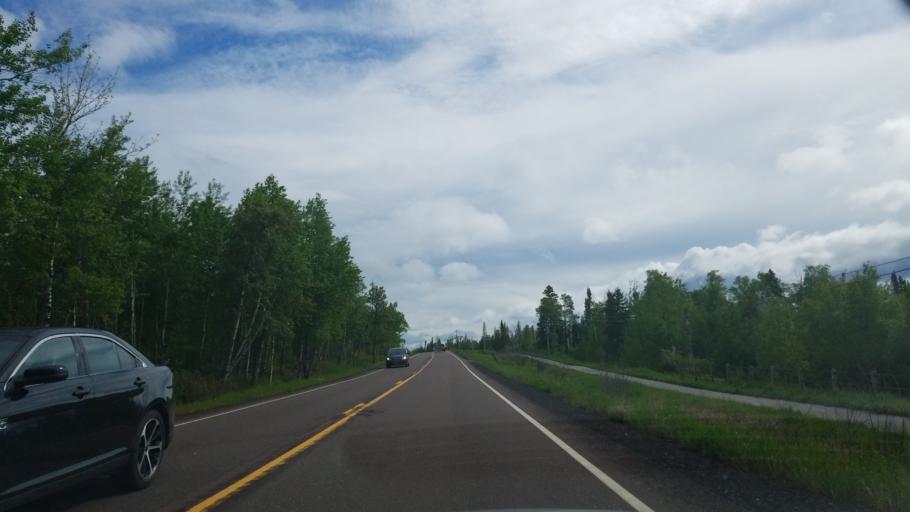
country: US
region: Minnesota
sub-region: Lake County
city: Silver Bay
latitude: 47.1538
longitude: -91.4458
